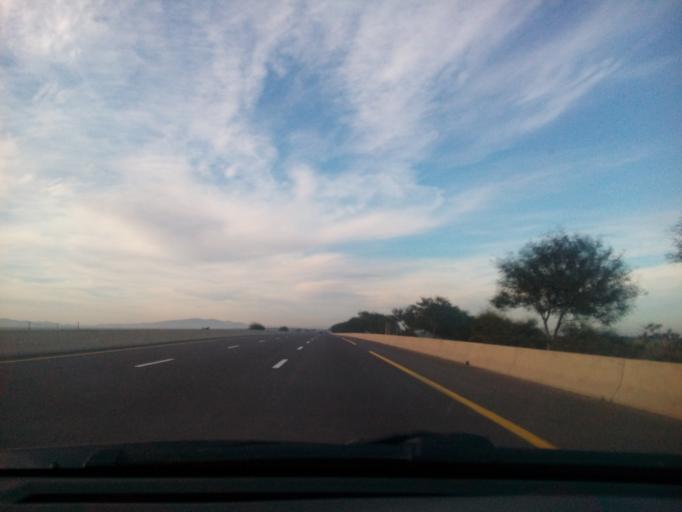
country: DZ
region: Mostaganem
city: Mostaganem
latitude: 35.6935
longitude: 0.1737
